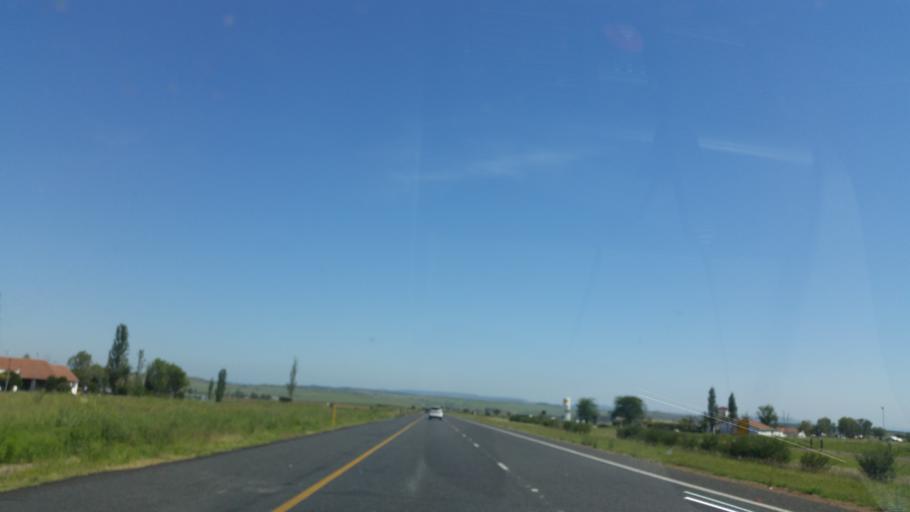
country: ZA
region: KwaZulu-Natal
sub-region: uThukela District Municipality
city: Estcourt
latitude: -28.9262
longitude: 29.7816
